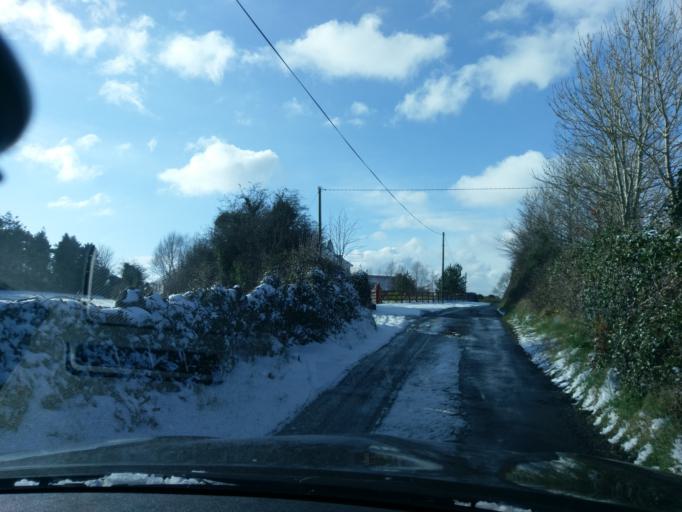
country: IE
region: Connaught
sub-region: County Galway
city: Athenry
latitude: 53.2054
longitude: -8.8115
